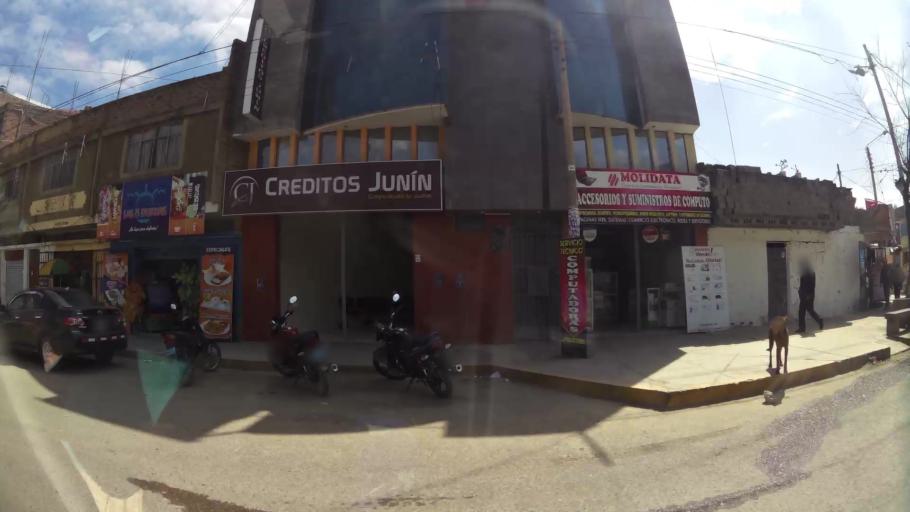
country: PE
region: Junin
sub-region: Provincia de Huancayo
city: Huancayo
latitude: -12.0857
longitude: -75.2076
